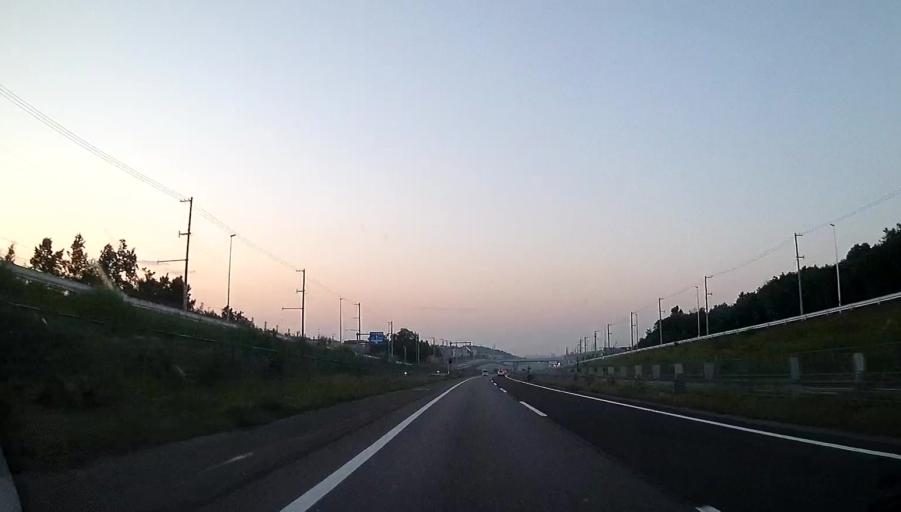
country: JP
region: Hokkaido
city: Kitahiroshima
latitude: 42.9869
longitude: 141.4708
